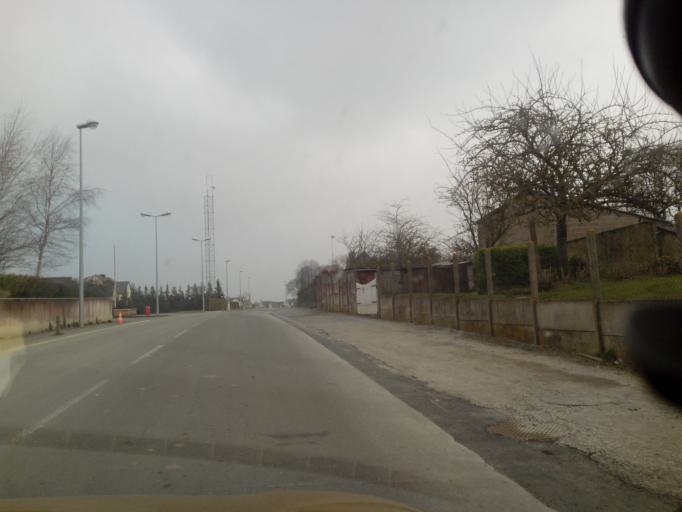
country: FR
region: Brittany
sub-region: Departement d'Ille-et-Vilaine
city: Saint-Meen-le-Grand
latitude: 48.1929
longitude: -2.1952
